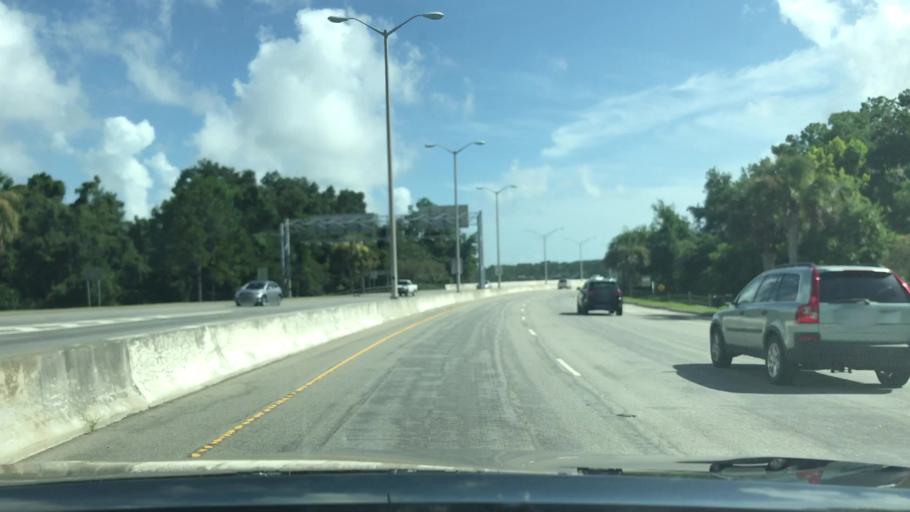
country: US
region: South Carolina
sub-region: Beaufort County
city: Hilton Head Island
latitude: 32.1849
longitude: -80.7655
